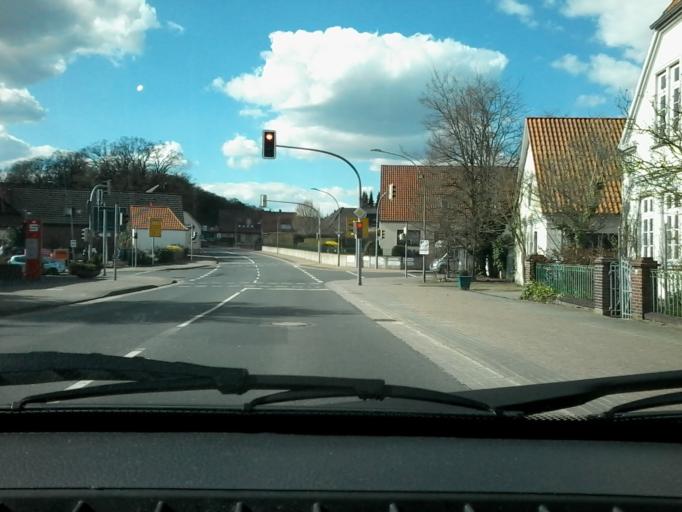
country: DE
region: Lower Saxony
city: Ahsen-Oetzen
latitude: 52.9949
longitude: 9.1168
